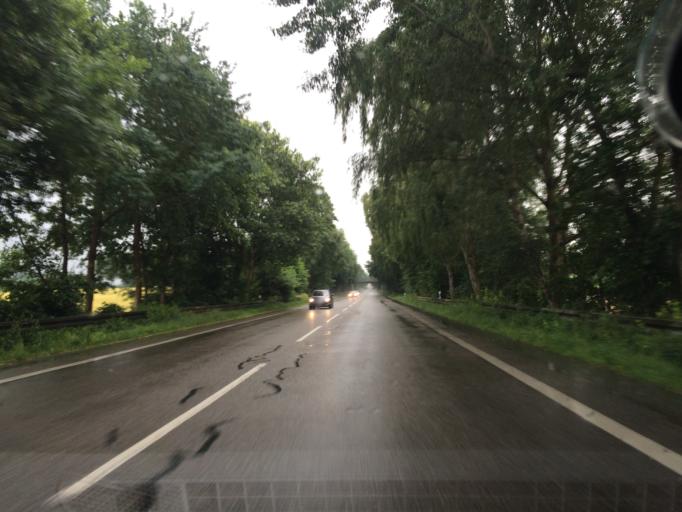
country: DE
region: North Rhine-Westphalia
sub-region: Regierungsbezirk Munster
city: Haltern
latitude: 51.7730
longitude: 7.2036
